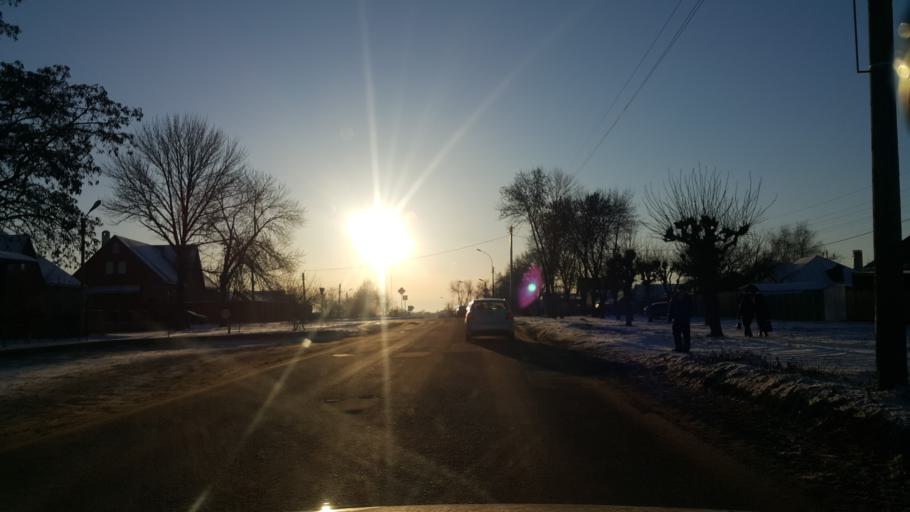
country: RU
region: Tambov
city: Pokrovo-Prigorodnoye
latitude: 52.7072
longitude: 41.4142
